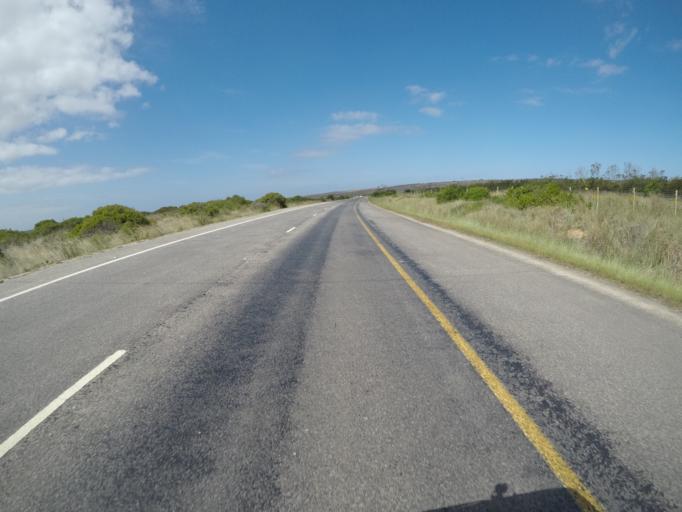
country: ZA
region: Western Cape
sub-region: Eden District Municipality
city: Mossel Bay
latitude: -34.1821
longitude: 22.0494
